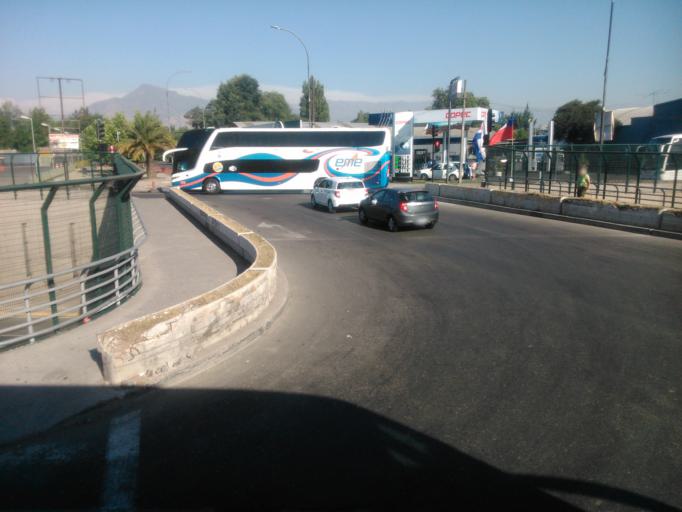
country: CL
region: Santiago Metropolitan
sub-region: Provincia de Maipo
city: Buin
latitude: -33.7332
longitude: -70.7340
